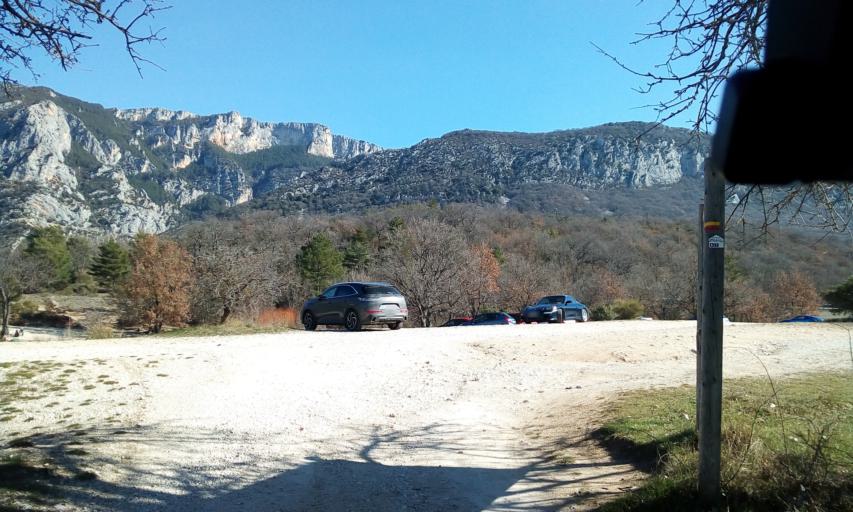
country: FR
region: Provence-Alpes-Cote d'Azur
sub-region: Departement des Alpes-de-Haute-Provence
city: Riez
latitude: 43.7965
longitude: 6.2353
